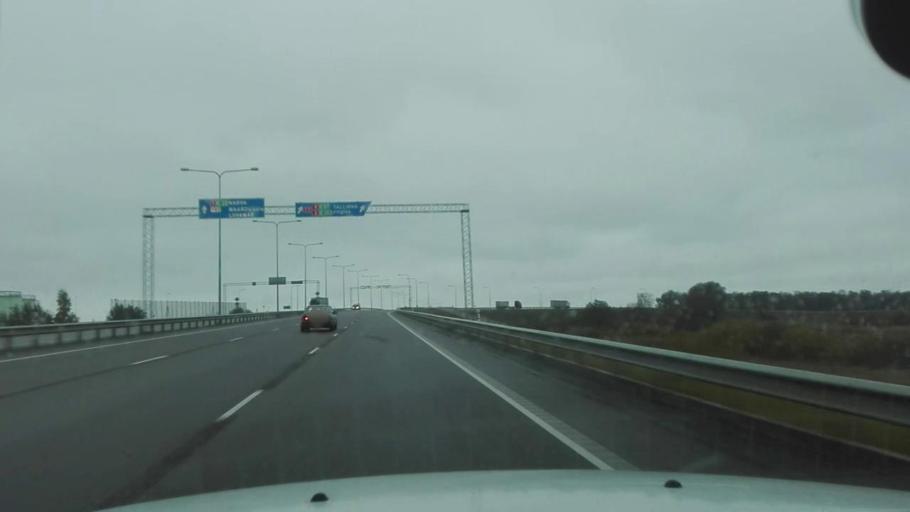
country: EE
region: Harju
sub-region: Joelaehtme vald
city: Loo
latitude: 59.4571
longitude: 24.9828
